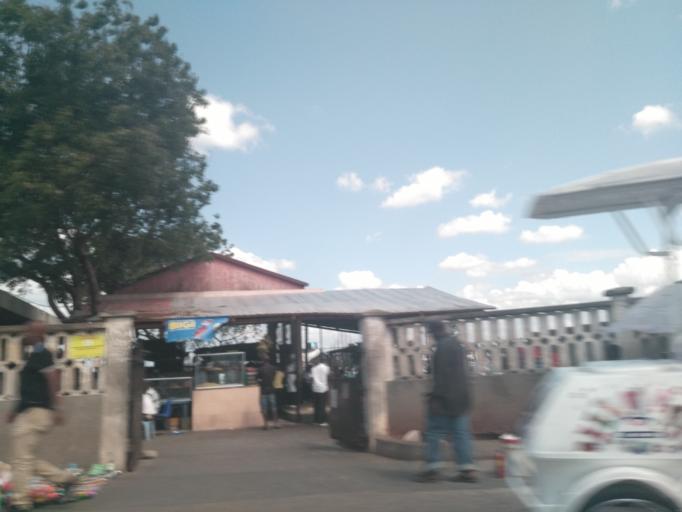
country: TZ
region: Dar es Salaam
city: Dar es Salaam
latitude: -6.8195
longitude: 39.2995
